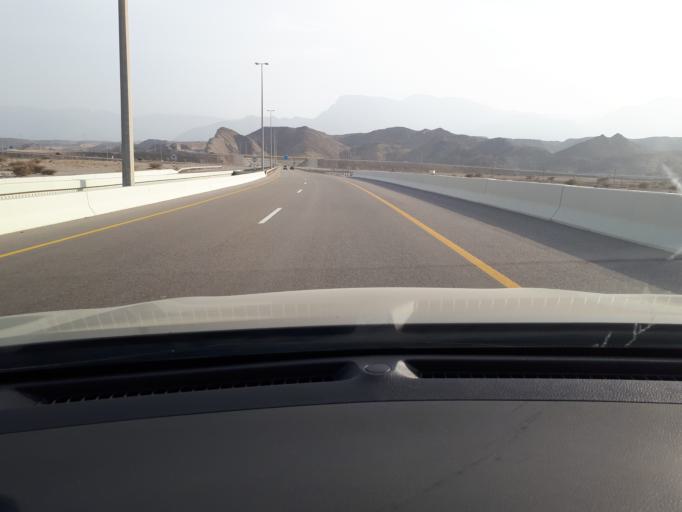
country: OM
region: Muhafazat Masqat
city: Muscat
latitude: 23.2064
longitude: 58.8839
